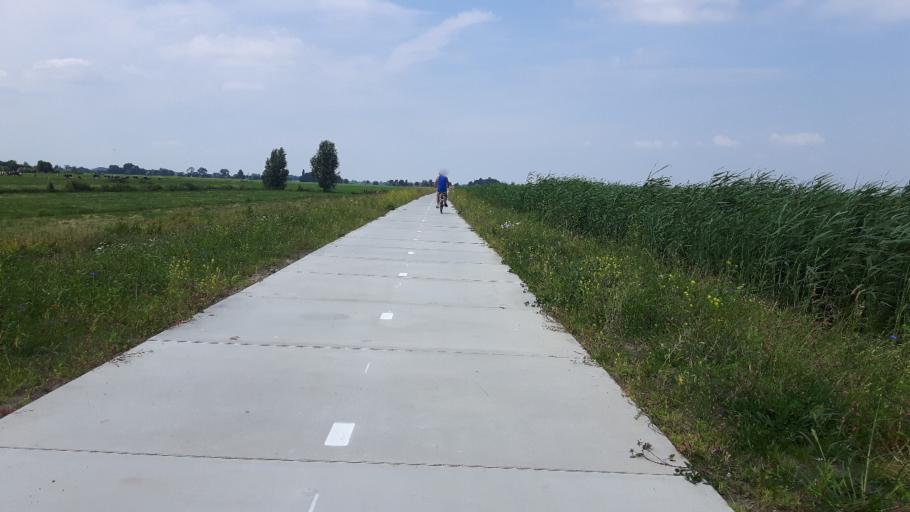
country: NL
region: South Holland
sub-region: Molenwaard
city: Liesveld
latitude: 51.8931
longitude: 4.8559
